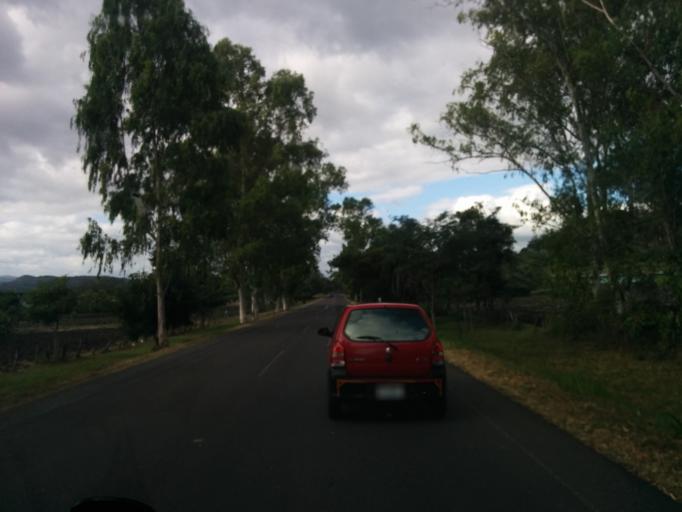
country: NI
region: Esteli
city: Esteli
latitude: 13.1488
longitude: -86.3689
